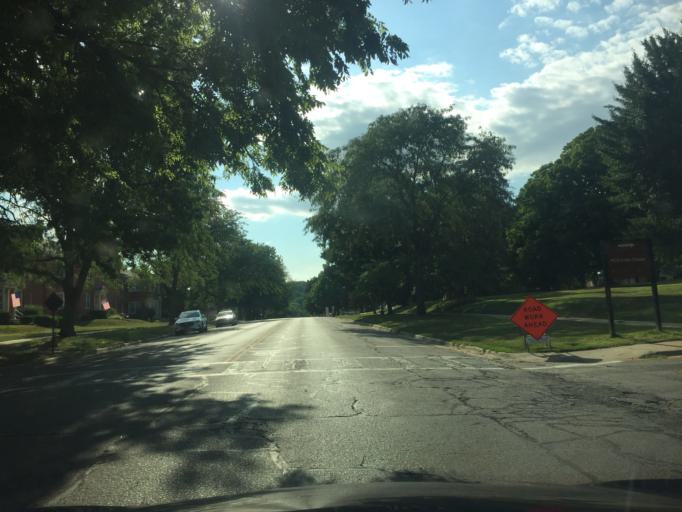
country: US
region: Kansas
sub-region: Leavenworth County
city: Leavenworth
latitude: 39.3527
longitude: -94.9210
